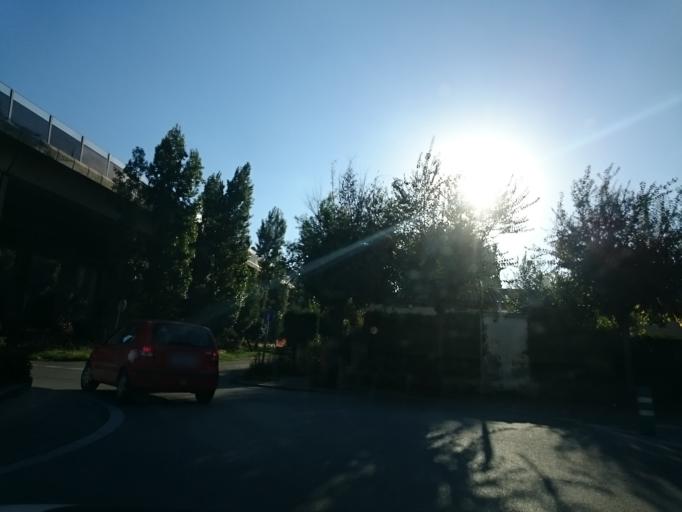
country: ES
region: Catalonia
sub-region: Provincia de Barcelona
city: Palleja
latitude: 41.4152
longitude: 1.9999
